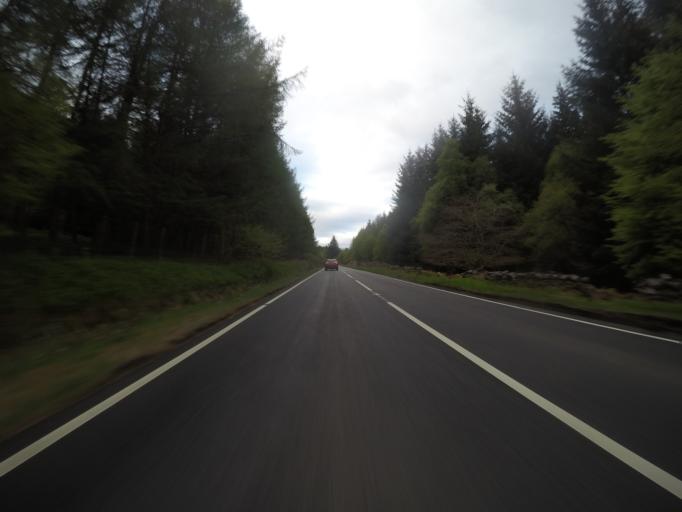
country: GB
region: Scotland
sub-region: Highland
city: Spean Bridge
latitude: 57.1131
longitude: -4.7118
